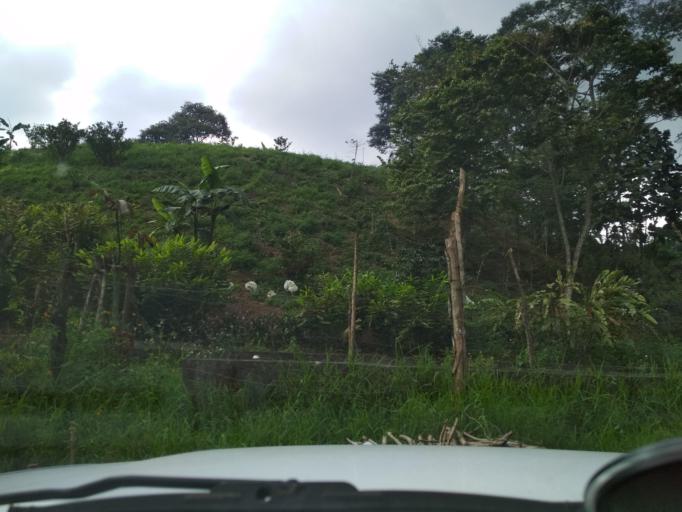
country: MX
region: Veracruz
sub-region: Fortin
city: Santa Lucia Potrerillo
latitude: 18.9571
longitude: -97.0497
